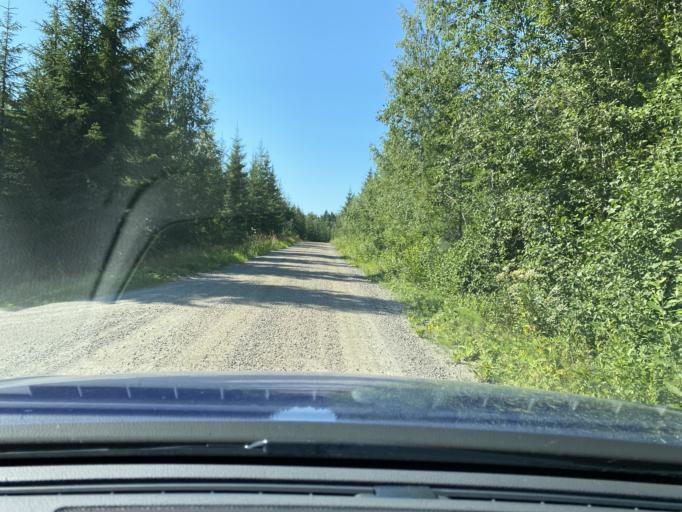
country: FI
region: Central Finland
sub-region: Jaemsae
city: Jaemsae
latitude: 61.8556
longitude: 25.3924
